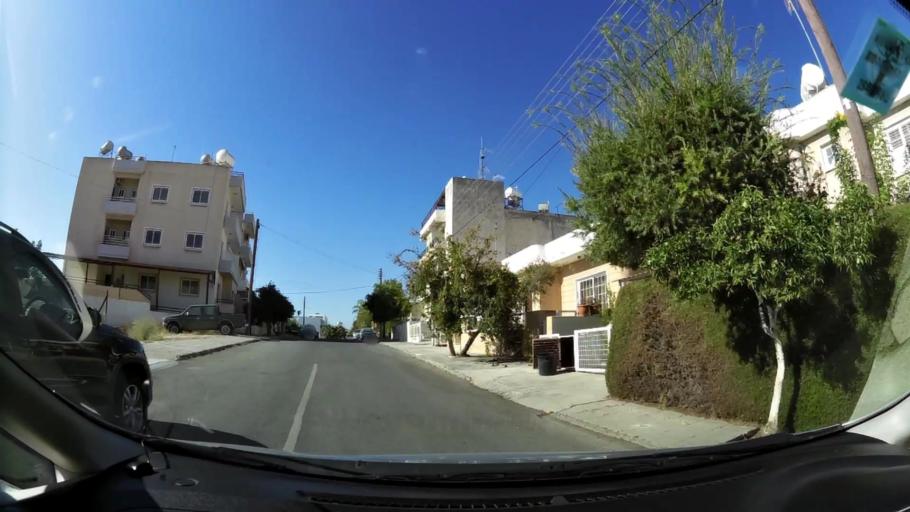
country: CY
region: Larnaka
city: Larnaca
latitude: 34.9333
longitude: 33.6168
